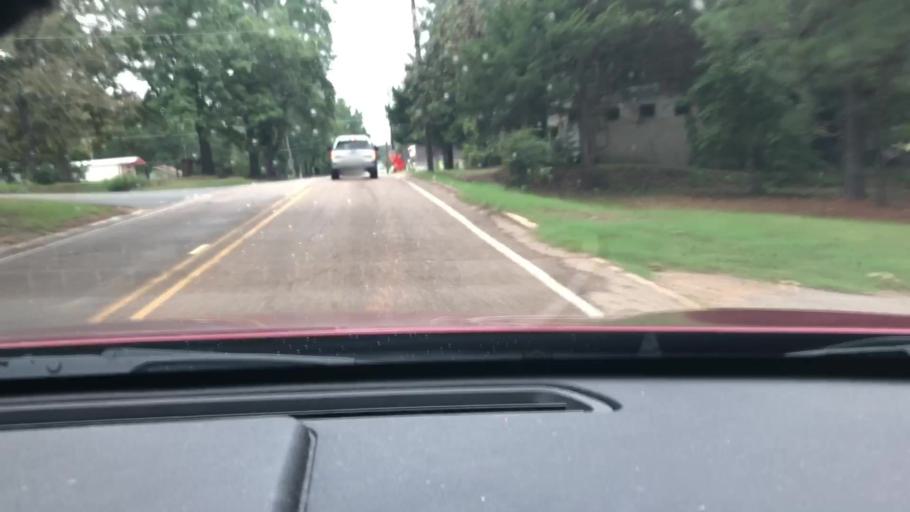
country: US
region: Arkansas
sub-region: Lafayette County
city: Stamps
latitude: 33.3658
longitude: -93.5065
